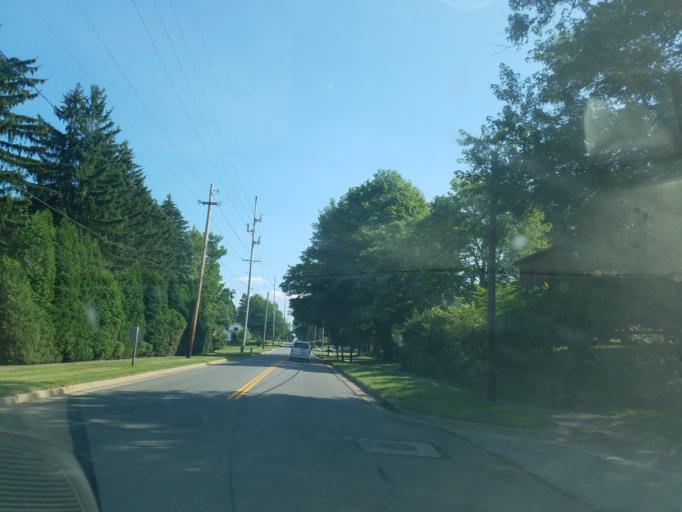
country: US
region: Ohio
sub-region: Summit County
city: Mogadore
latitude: 41.0455
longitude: -81.3930
